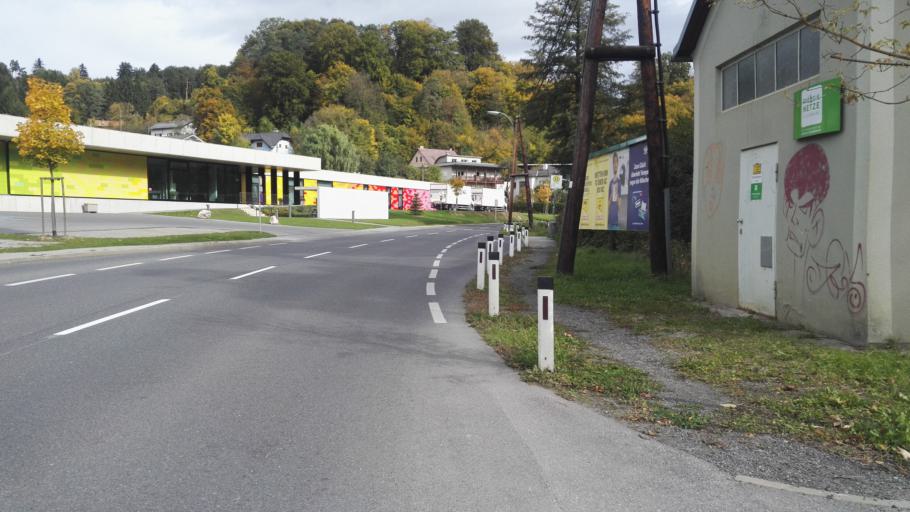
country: AT
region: Styria
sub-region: Graz Stadt
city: Mariatrost
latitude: 47.0871
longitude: 15.4740
